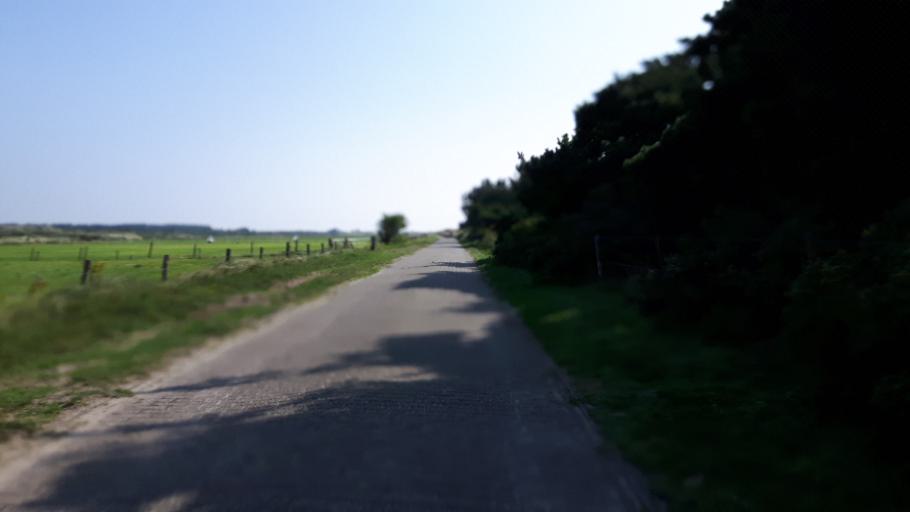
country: NL
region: Friesland
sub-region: Gemeente Ameland
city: Nes
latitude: 53.4554
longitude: 5.8056
